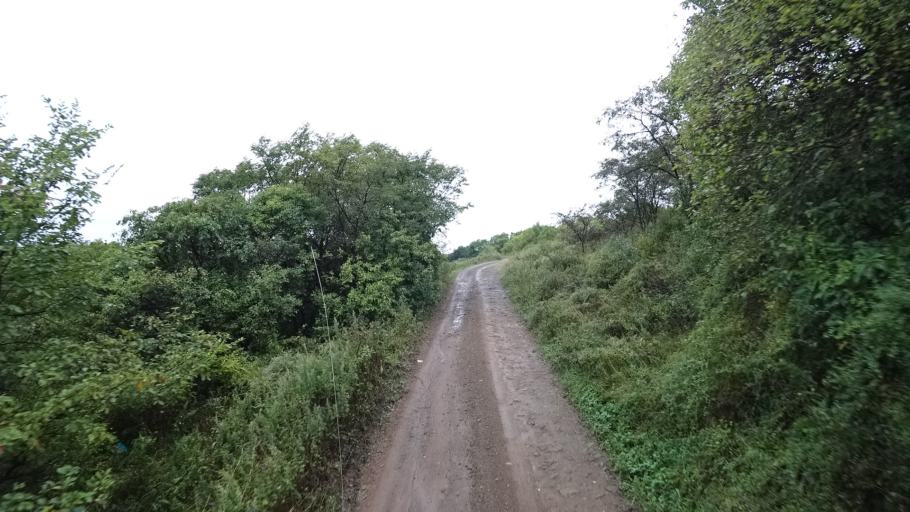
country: RU
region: Primorskiy
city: Monastyrishche
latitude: 44.2680
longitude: 132.4037
